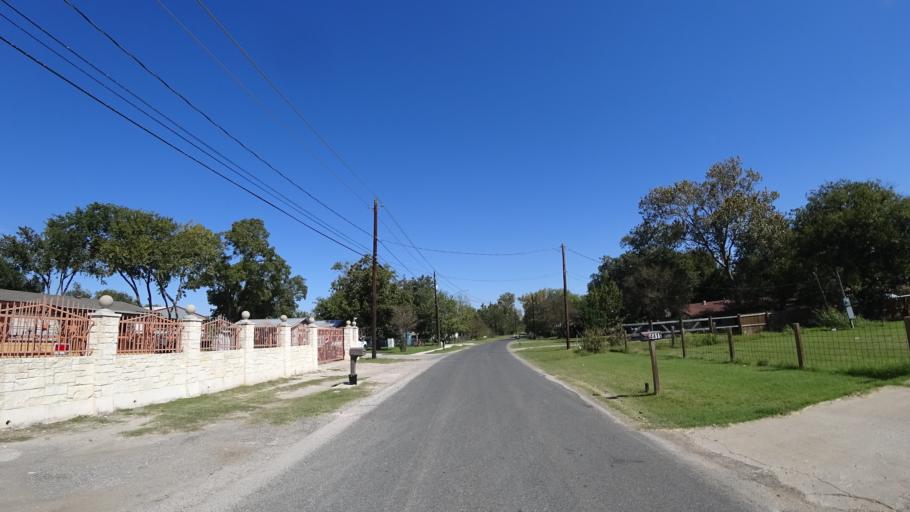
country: US
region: Texas
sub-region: Travis County
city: Austin
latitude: 30.1879
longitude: -97.6879
